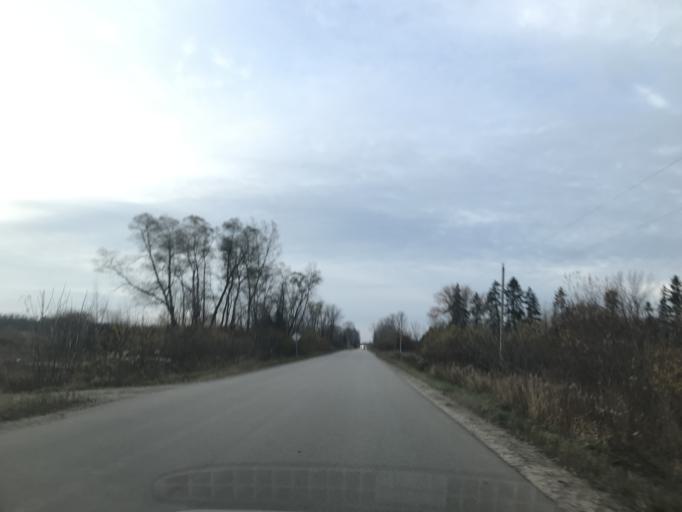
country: US
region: Wisconsin
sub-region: Marinette County
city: Peshtigo
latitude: 45.0912
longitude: -87.7995
